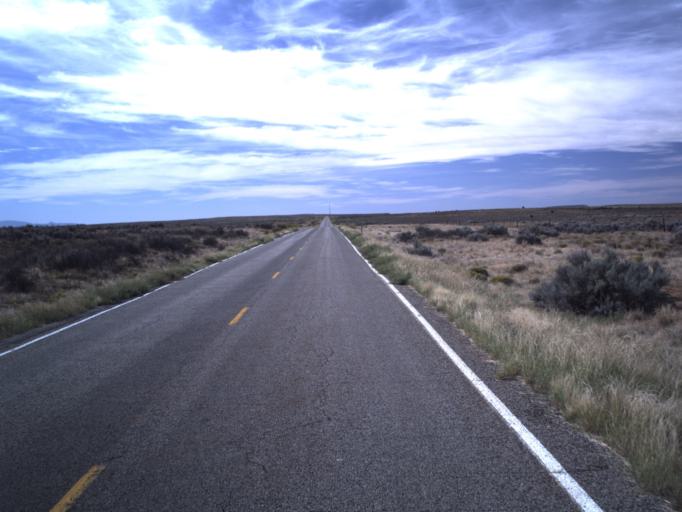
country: US
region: Utah
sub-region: San Juan County
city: Blanding
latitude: 37.3722
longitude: -109.3431
